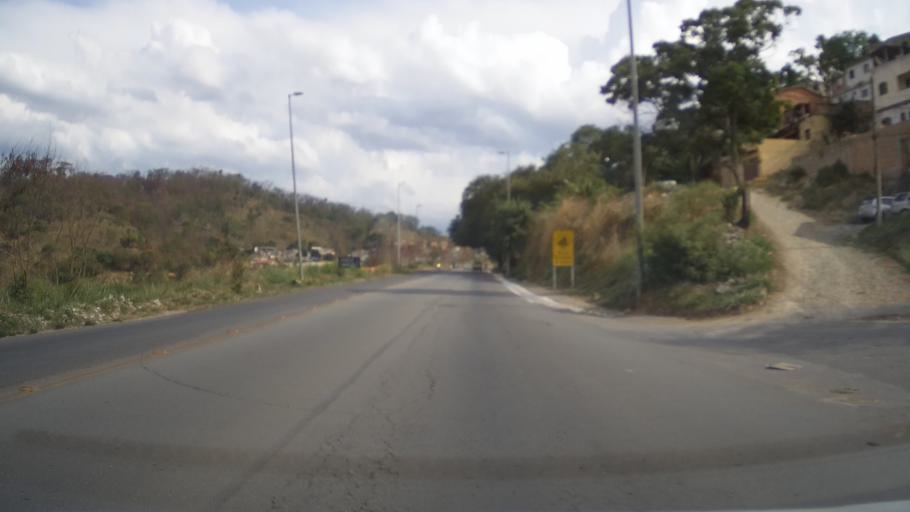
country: BR
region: Minas Gerais
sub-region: Belo Horizonte
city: Belo Horizonte
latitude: -19.8722
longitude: -43.8937
